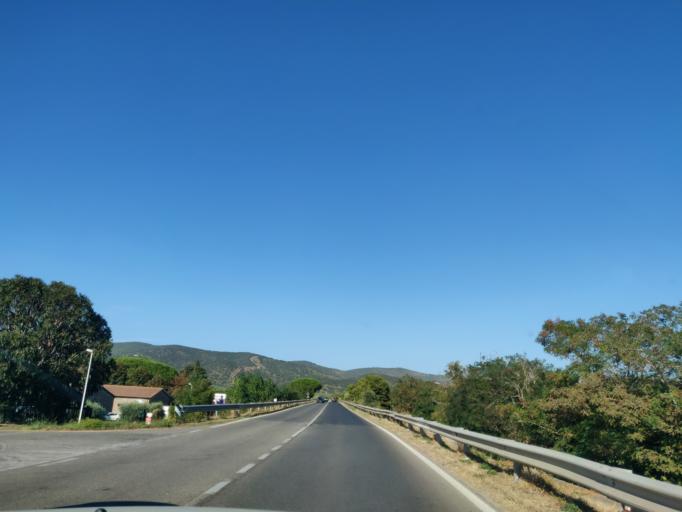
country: IT
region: Tuscany
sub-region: Provincia di Grosseto
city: Orbetello Scalo
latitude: 42.4457
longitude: 11.2399
